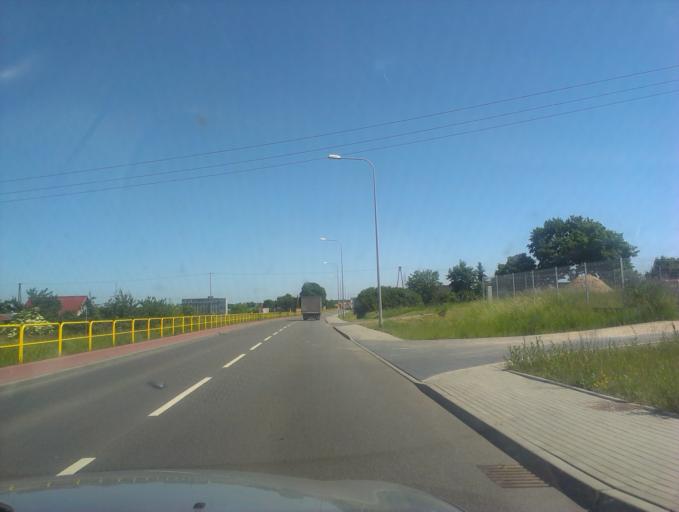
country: PL
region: Pomeranian Voivodeship
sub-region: Powiat chojnicki
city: Chojnice
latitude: 53.6882
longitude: 17.6244
